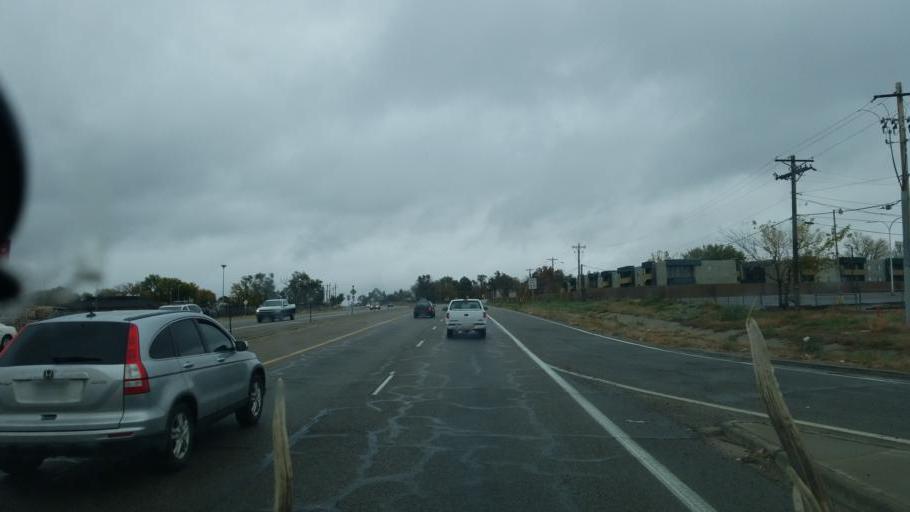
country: US
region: Colorado
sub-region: Pueblo County
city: Pueblo
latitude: 38.2866
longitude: -104.5969
